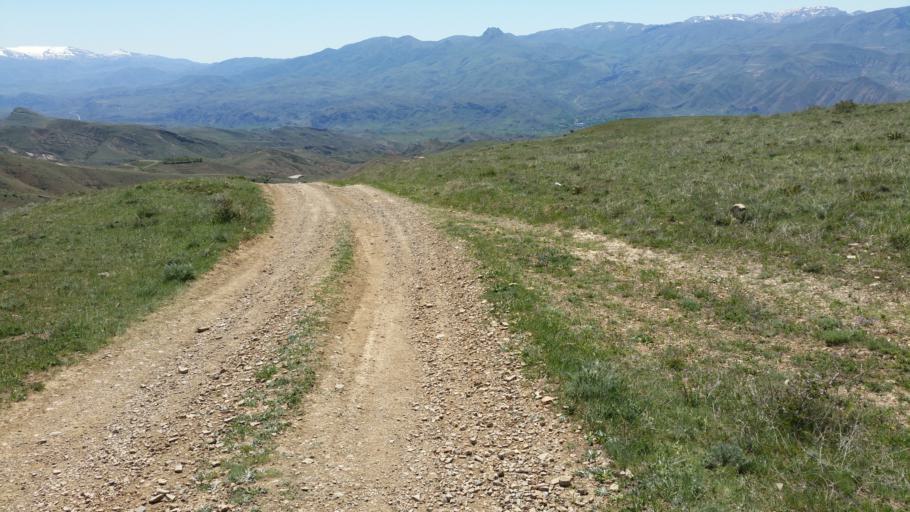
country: AM
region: Vayots' Dzori Marz
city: Vernashen
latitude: 39.8014
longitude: 45.3605
